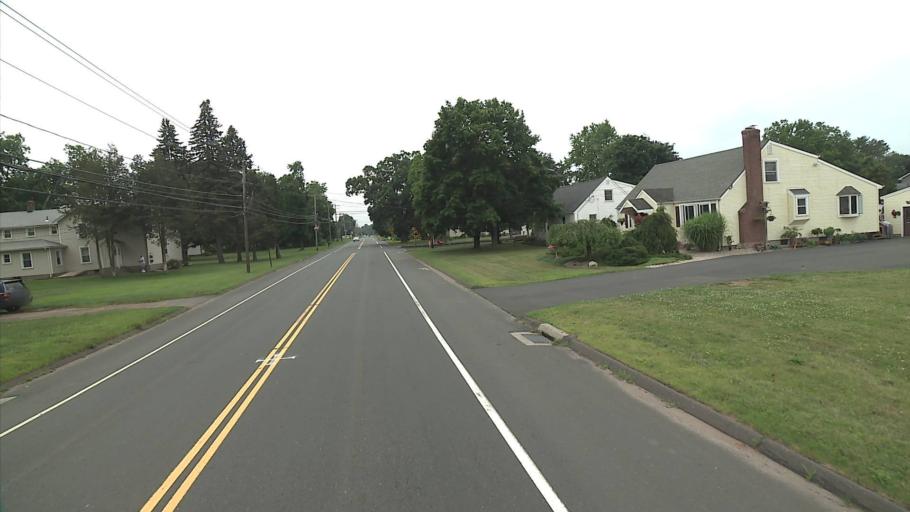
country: US
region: Connecticut
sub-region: Middlesex County
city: Cromwell
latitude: 41.6314
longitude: -72.6502
